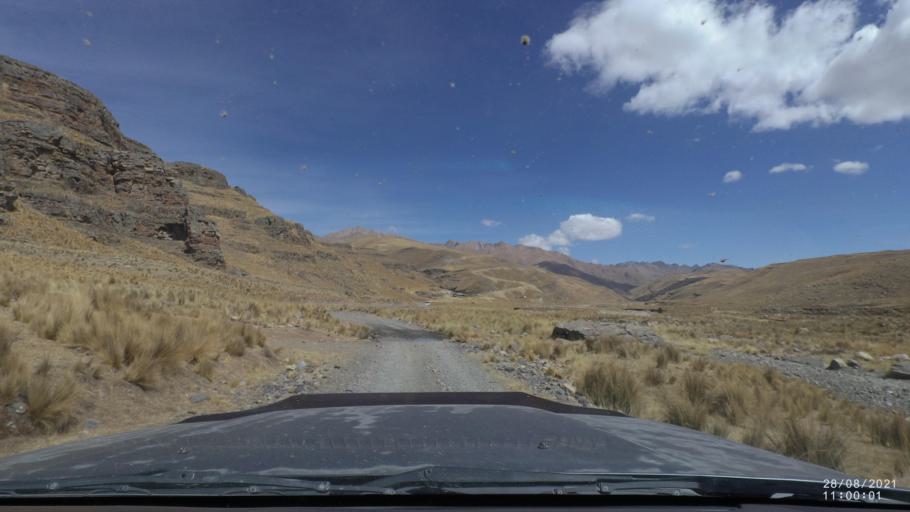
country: BO
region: Cochabamba
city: Cochabamba
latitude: -17.1829
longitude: -66.2583
